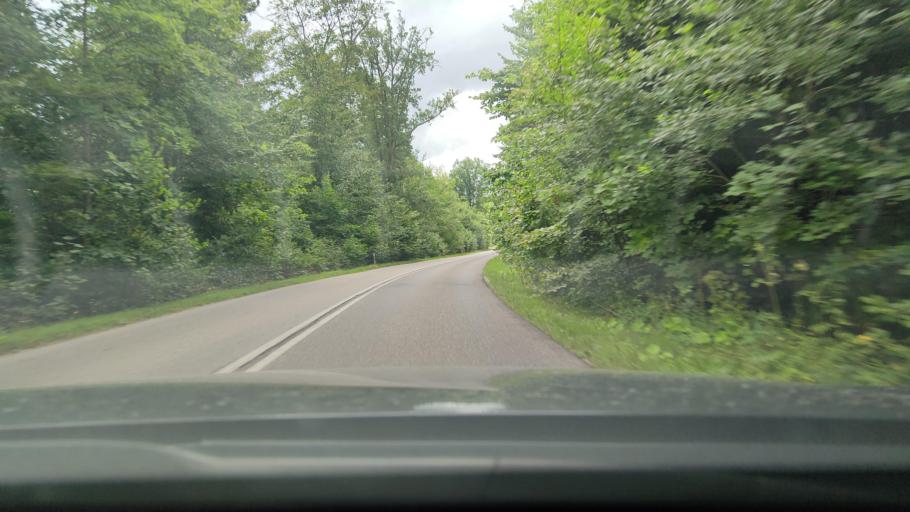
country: PL
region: Pomeranian Voivodeship
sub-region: Powiat pucki
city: Krokowa
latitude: 54.7454
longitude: 18.1694
